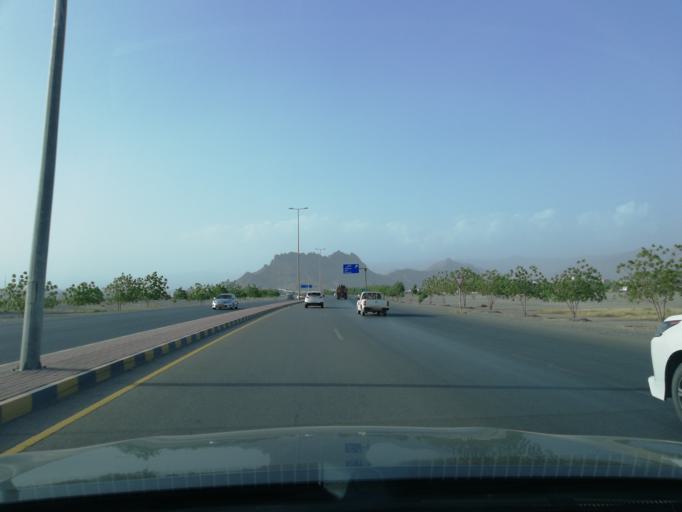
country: OM
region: Muhafazat ad Dakhiliyah
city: Nizwa
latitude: 22.8511
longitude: 57.5403
